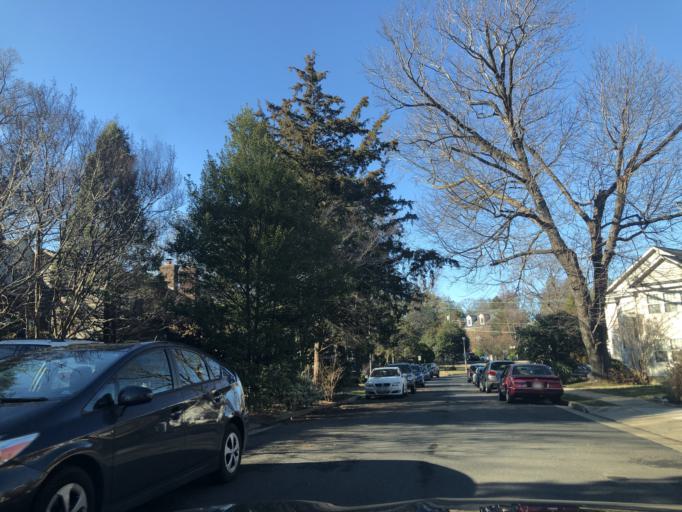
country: US
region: Virginia
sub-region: Arlington County
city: Arlington
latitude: 38.8845
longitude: -77.1228
